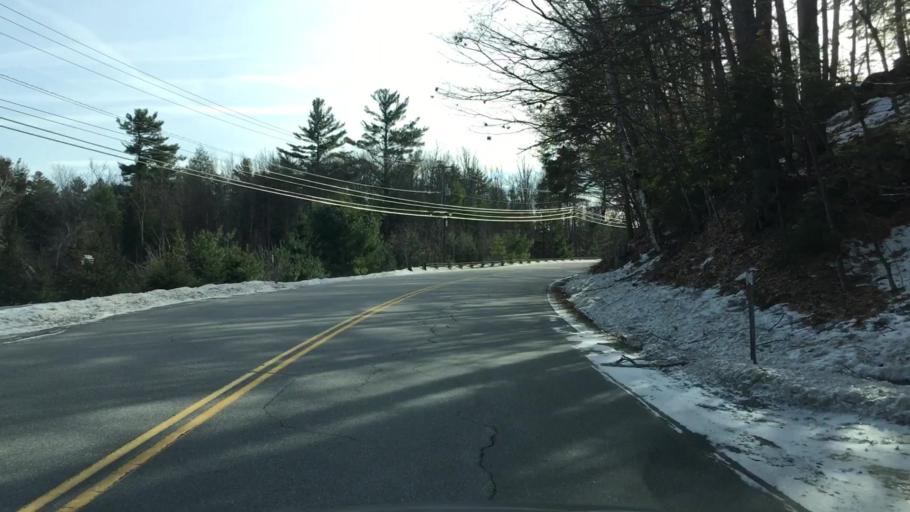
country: US
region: New Hampshire
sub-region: Sullivan County
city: Sunapee
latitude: 43.4373
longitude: -72.0651
